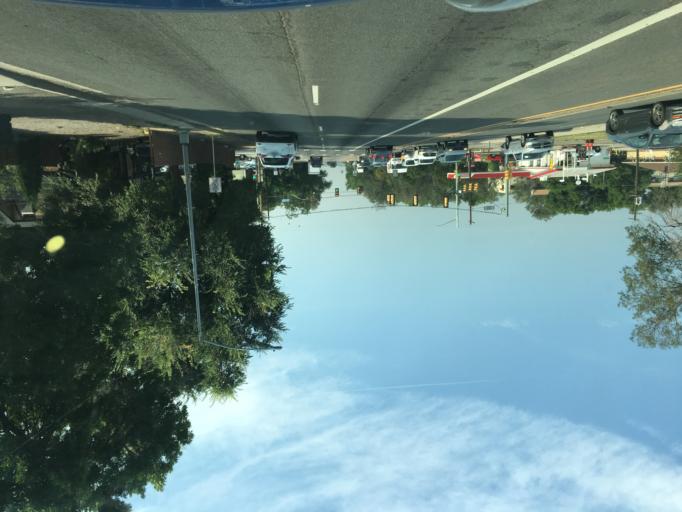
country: US
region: Colorado
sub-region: Jefferson County
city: Wheat Ridge
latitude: 39.7611
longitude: -105.0814
